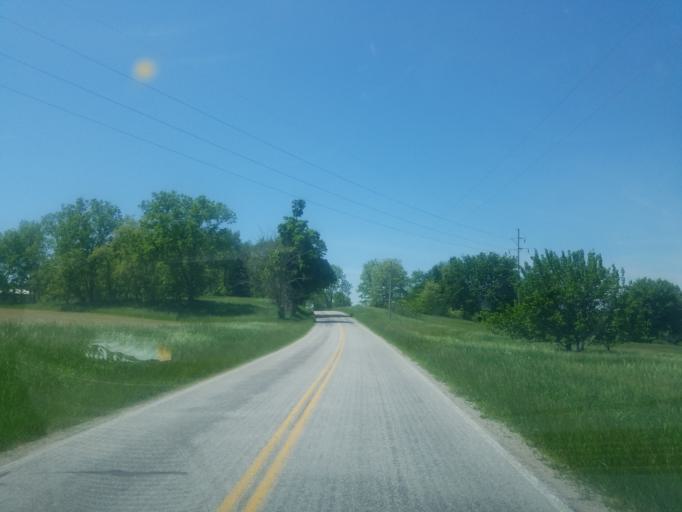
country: US
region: Ohio
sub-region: Huron County
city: New London
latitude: 41.1144
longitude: -82.4440
